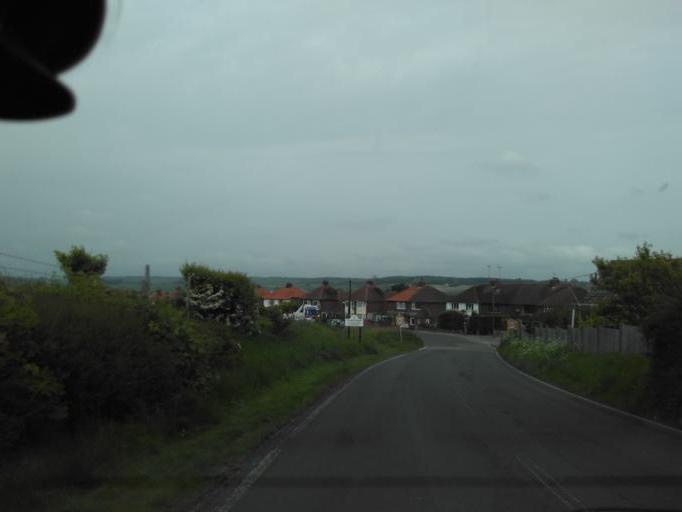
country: GB
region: England
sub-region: Kent
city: Chartham
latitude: 51.2486
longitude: 1.0186
